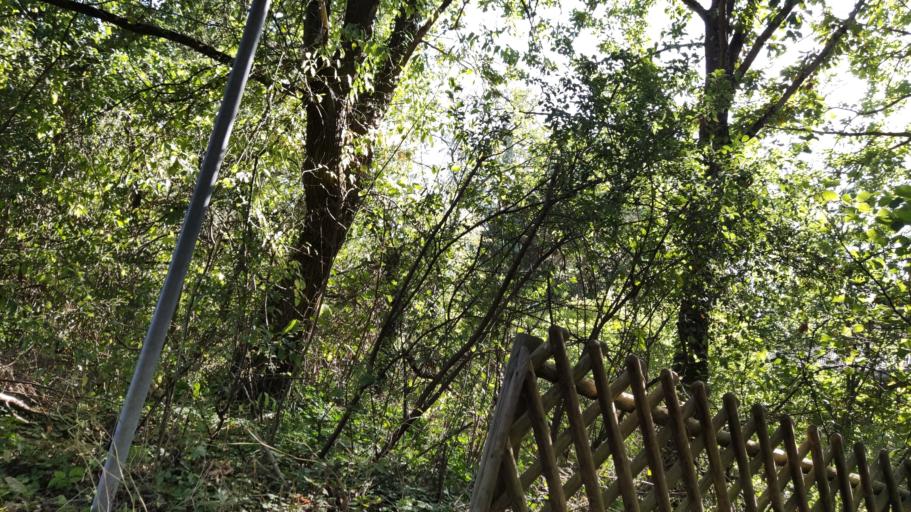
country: DE
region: Lower Saxony
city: Wendisch Evern
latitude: 53.2178
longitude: 10.4946
